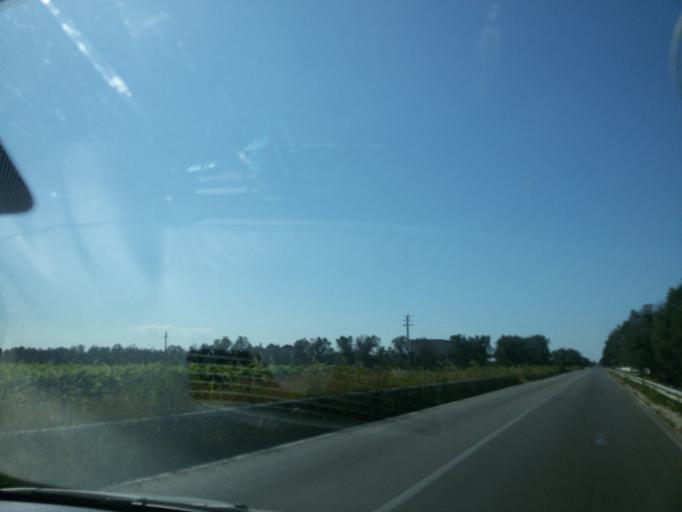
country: IT
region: Apulia
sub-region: Provincia di Brindisi
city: San Donaci
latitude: 40.4577
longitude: 17.9129
